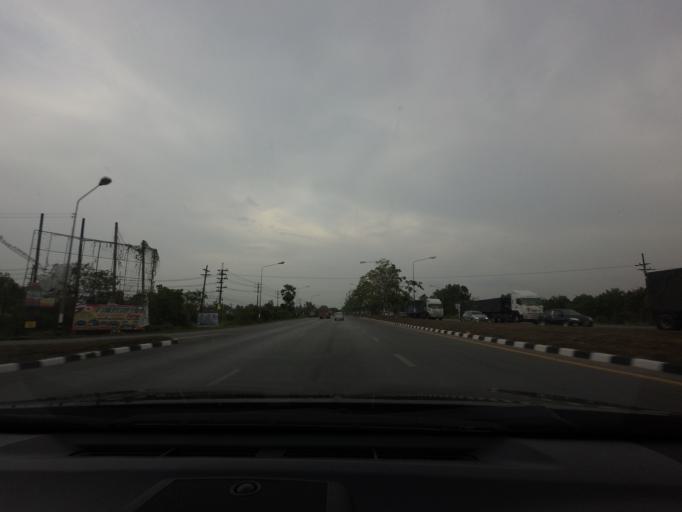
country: TH
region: Surat Thani
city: Chaiya
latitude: 9.4124
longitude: 99.1611
